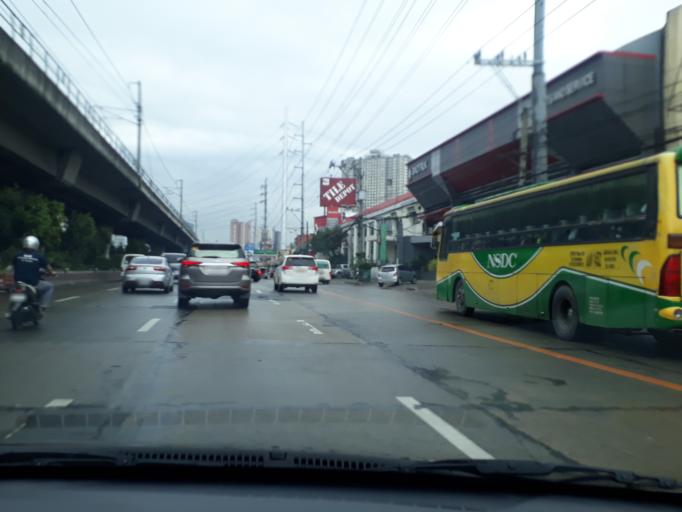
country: PH
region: Calabarzon
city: Del Monte
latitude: 14.6574
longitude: 121.0090
